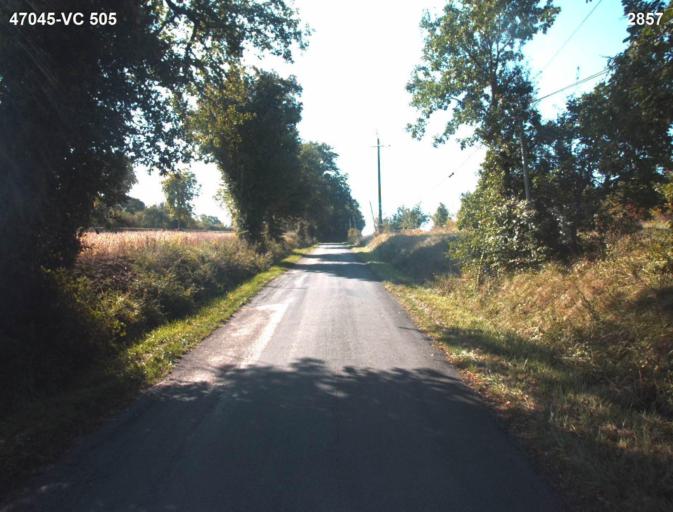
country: FR
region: Aquitaine
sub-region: Departement du Lot-et-Garonne
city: Nerac
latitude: 44.1393
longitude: 0.4162
